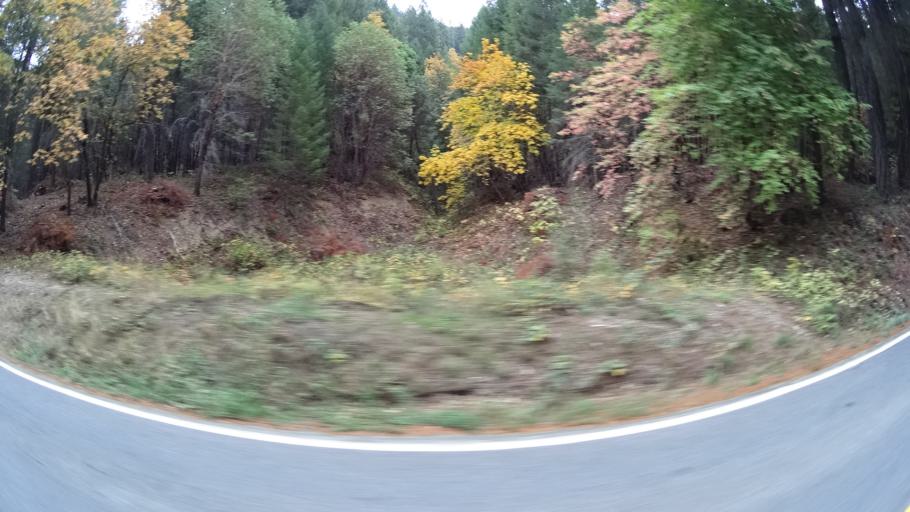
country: US
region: California
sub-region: Siskiyou County
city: Happy Camp
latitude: 41.8230
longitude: -123.3811
